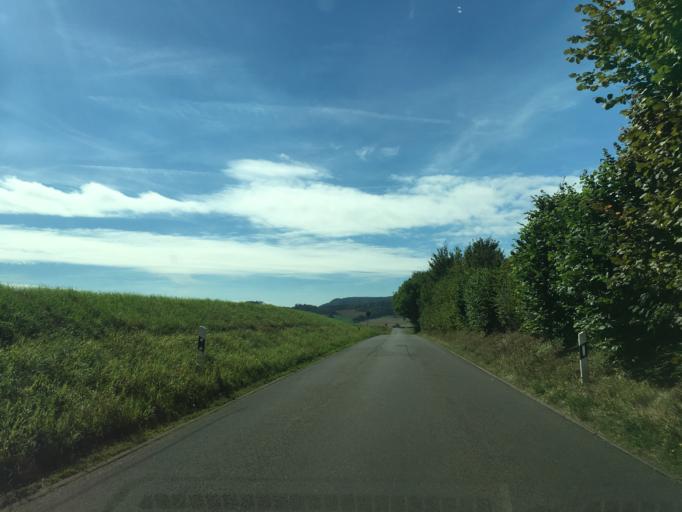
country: DE
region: Lower Saxony
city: Hameln
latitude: 52.0710
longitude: 9.3413
